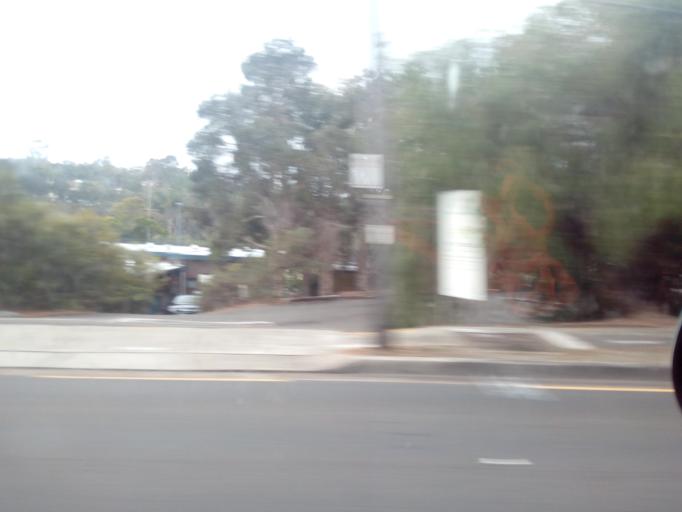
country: AU
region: New South Wales
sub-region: Willoughby
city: Castle Cove
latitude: -33.7873
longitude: 151.2016
